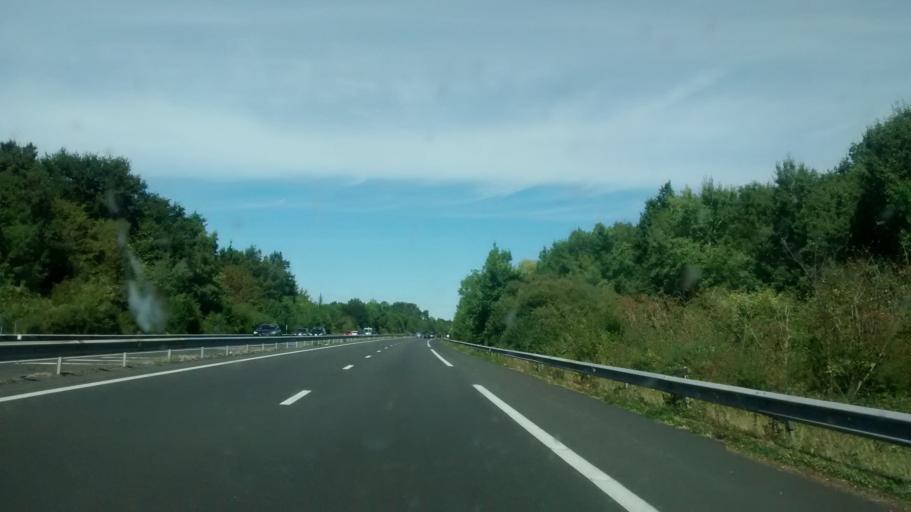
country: FR
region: Poitou-Charentes
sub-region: Departement de la Charente-Maritime
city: Thenac
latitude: 45.6480
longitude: -0.6315
